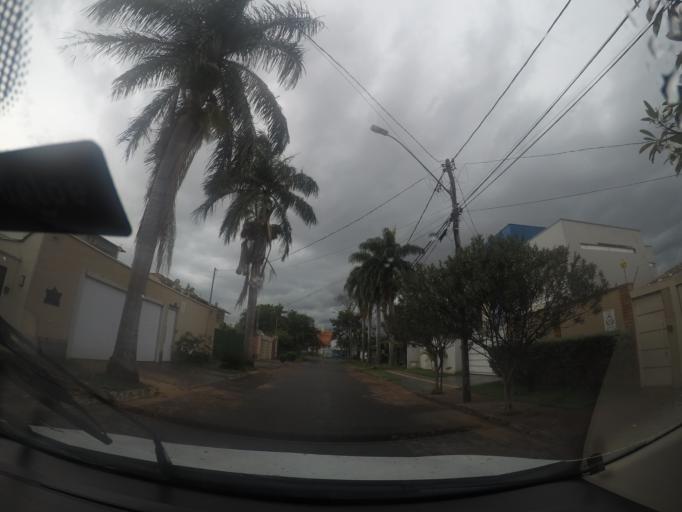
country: BR
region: Goias
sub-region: Goiania
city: Goiania
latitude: -16.6485
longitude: -49.2353
